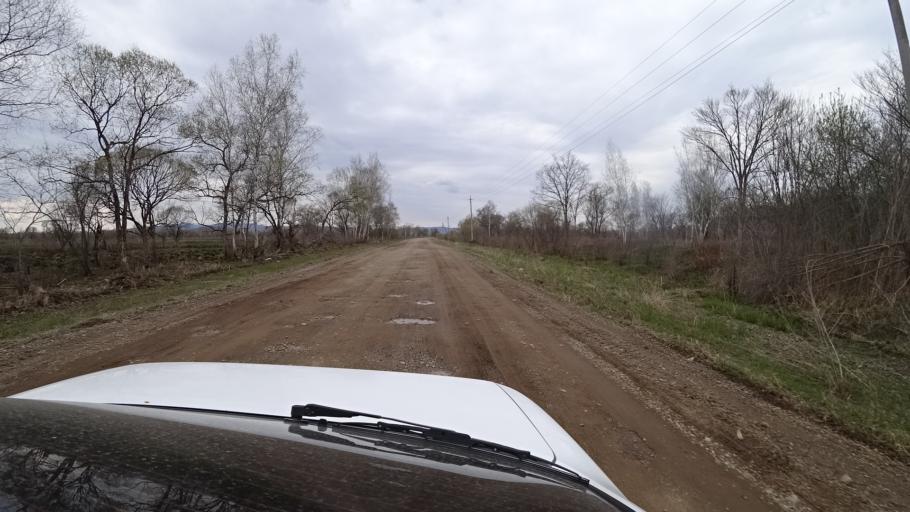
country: RU
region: Primorskiy
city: Novopokrovka
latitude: 45.5604
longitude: 134.3416
